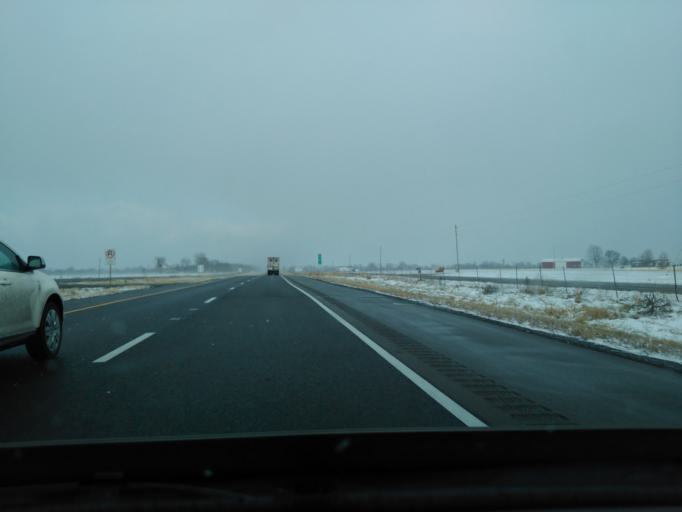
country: US
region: Illinois
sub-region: Madison County
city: Highland
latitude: 38.7938
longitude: -89.6130
